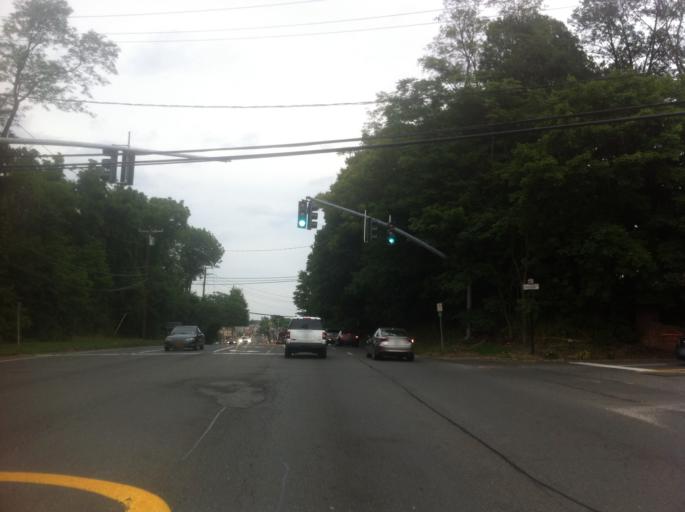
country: US
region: New York
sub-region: Nassau County
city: Greenvale
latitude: 40.8080
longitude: -73.6328
